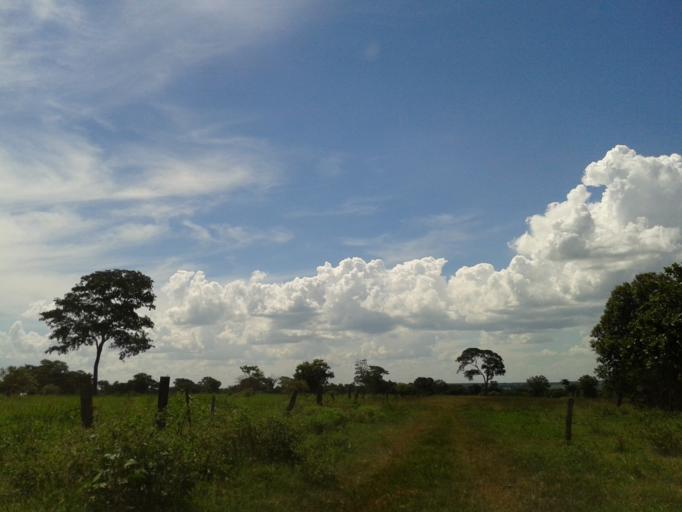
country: BR
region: Minas Gerais
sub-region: Santa Vitoria
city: Santa Vitoria
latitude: -19.1464
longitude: -50.5401
